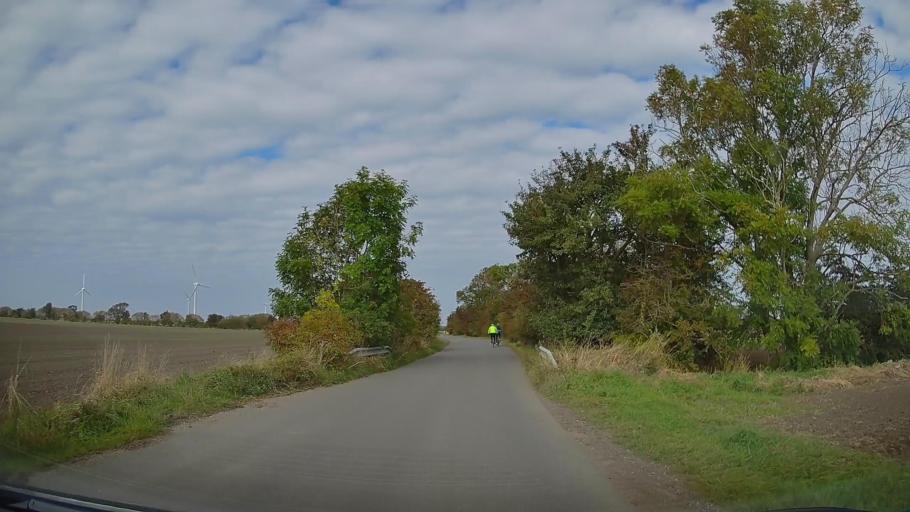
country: DE
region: Schleswig-Holstein
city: Grossenbrode
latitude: 54.4991
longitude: 11.0600
